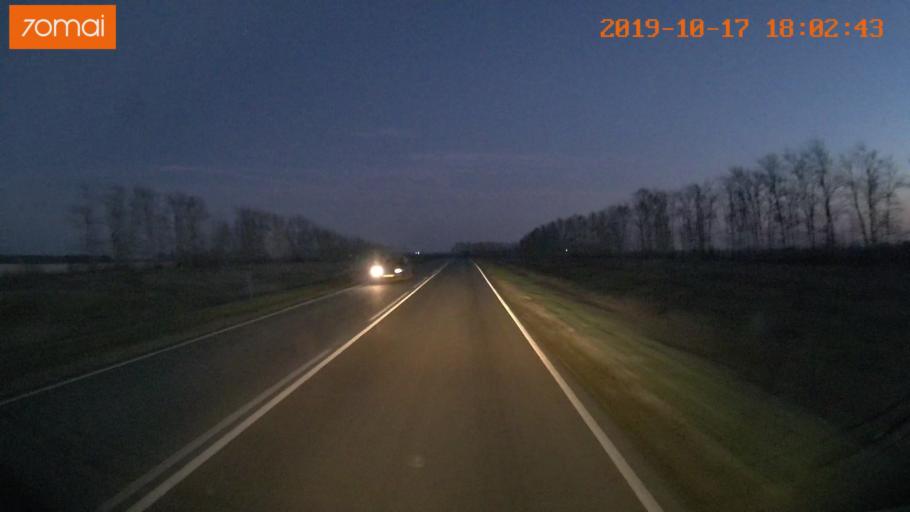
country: RU
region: Tula
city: Kurkino
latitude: 53.5036
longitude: 38.6171
